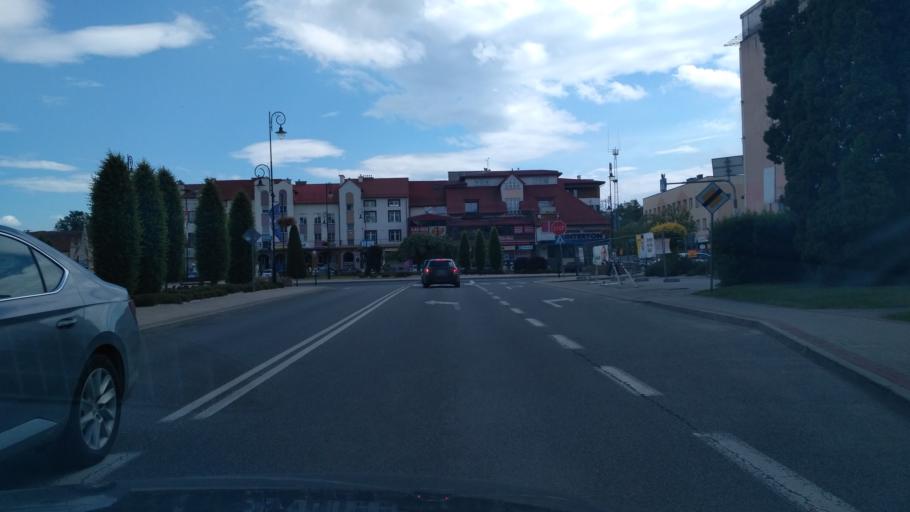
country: PL
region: Subcarpathian Voivodeship
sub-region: Powiat ropczycko-sedziszowski
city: Ropczyce
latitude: 50.0533
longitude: 21.6106
